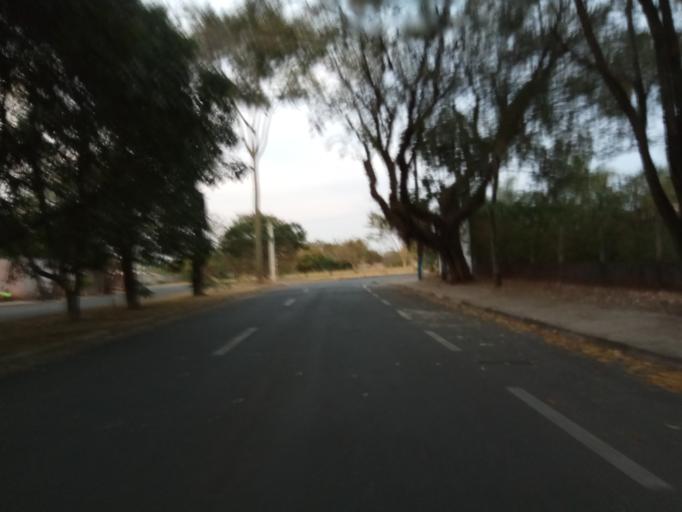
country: BR
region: Sao Paulo
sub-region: Piracicaba
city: Piracicaba
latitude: -22.7530
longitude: -47.5850
